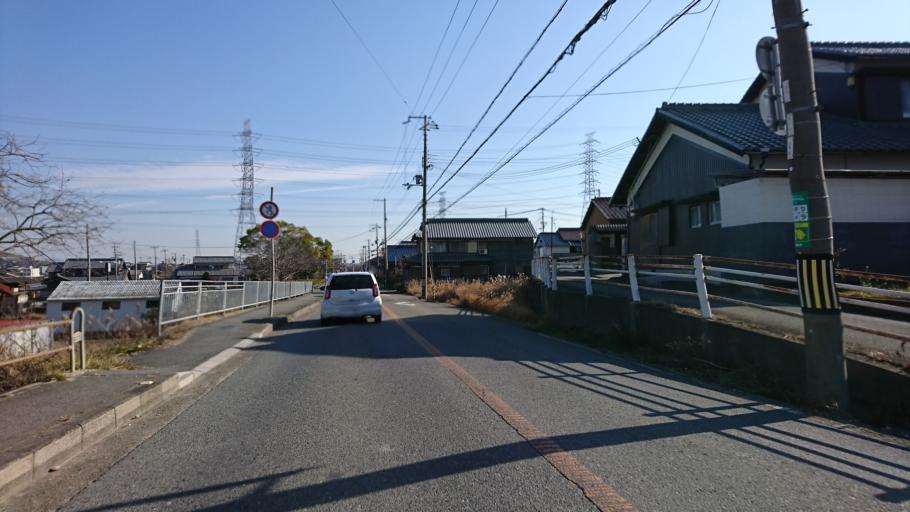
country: JP
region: Hyogo
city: Kakogawacho-honmachi
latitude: 34.8097
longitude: 134.8551
